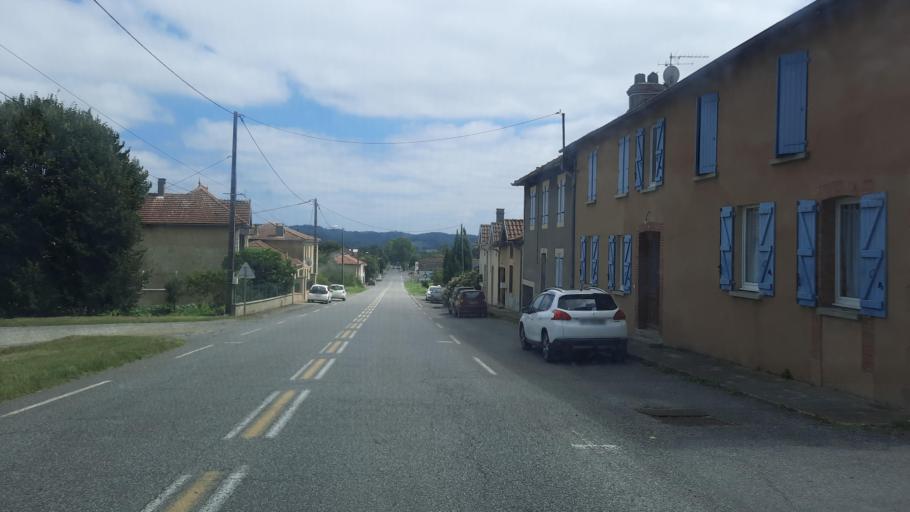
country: FR
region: Midi-Pyrenees
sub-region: Departement de la Haute-Garonne
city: Boulogne-sur-Gesse
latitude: 43.2948
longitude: 0.5123
